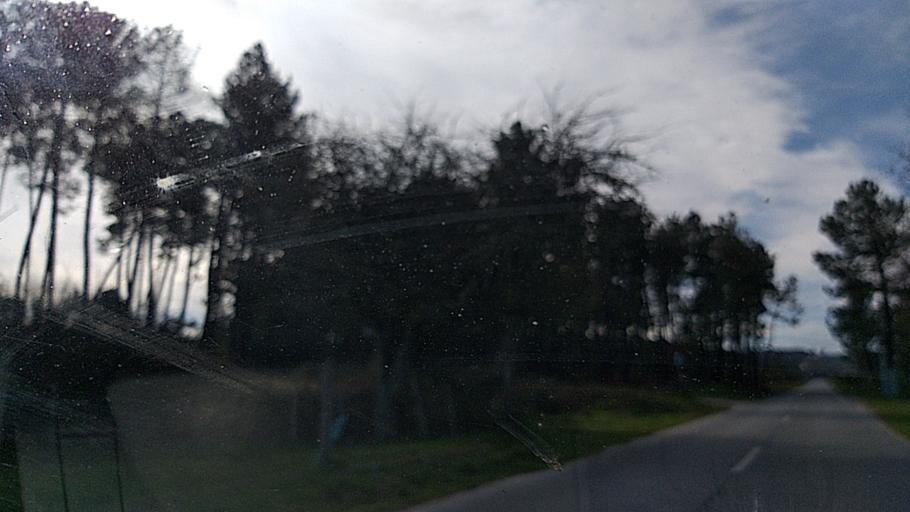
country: PT
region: Guarda
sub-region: Fornos de Algodres
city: Fornos de Algodres
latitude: 40.6669
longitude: -7.5298
